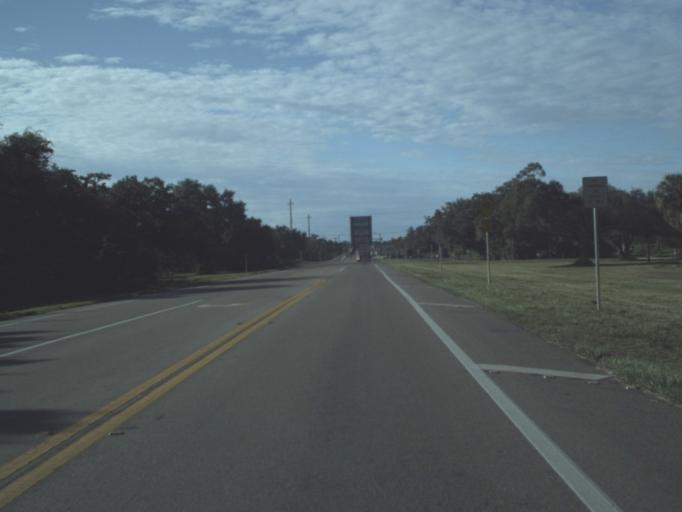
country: US
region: Florida
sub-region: Hendry County
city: LaBelle
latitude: 26.7740
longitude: -81.4375
